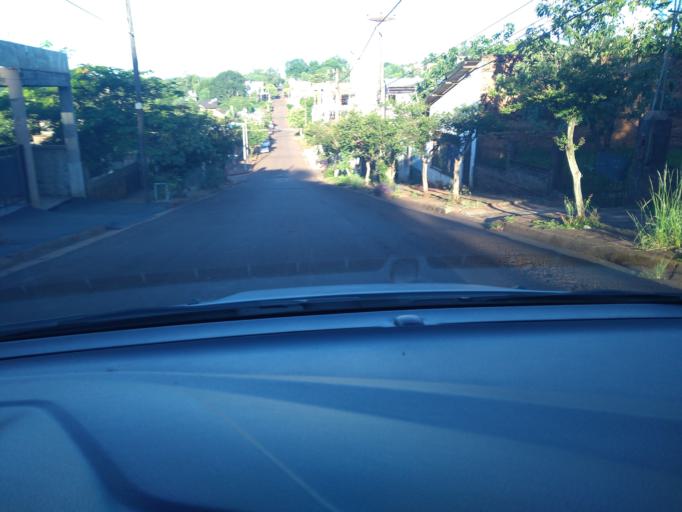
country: AR
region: Misiones
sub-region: Departamento de Obera
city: Obera
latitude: -27.4829
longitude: -55.1182
